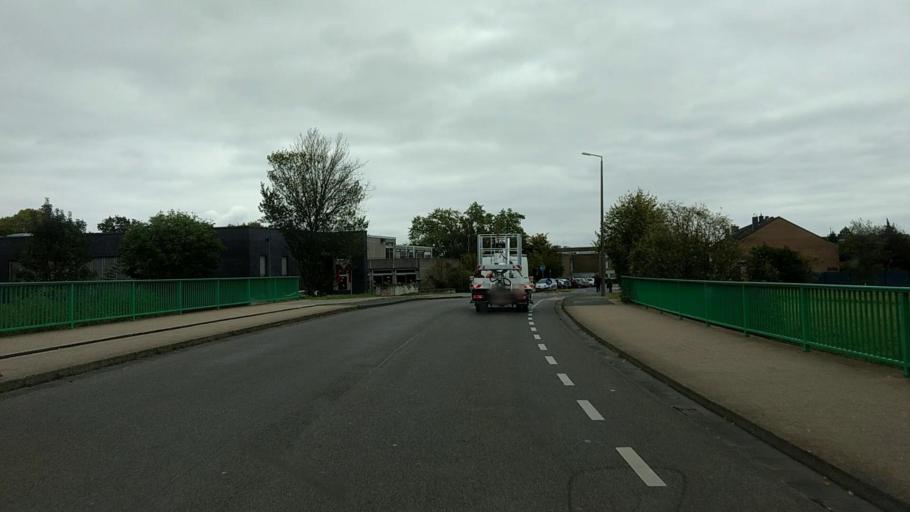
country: DE
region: North Rhine-Westphalia
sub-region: Regierungsbezirk Koln
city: Bergheim
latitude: 50.9488
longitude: 6.6307
